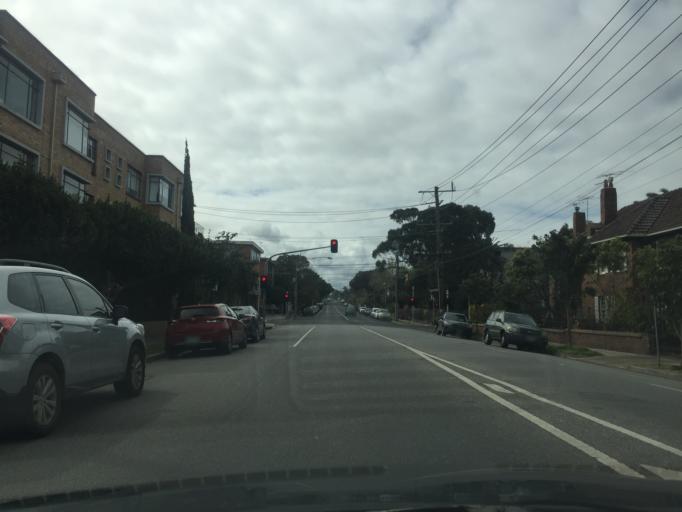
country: AU
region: Victoria
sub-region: Port Phillip
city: St Kilda East
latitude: -37.8620
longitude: 144.9959
